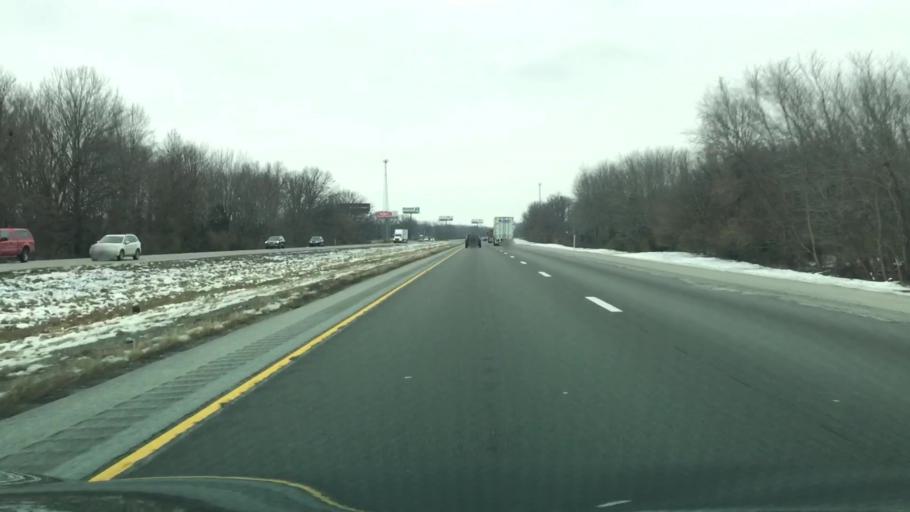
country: US
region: Illinois
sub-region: Jefferson County
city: Ina
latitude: 38.1951
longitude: -88.9064
